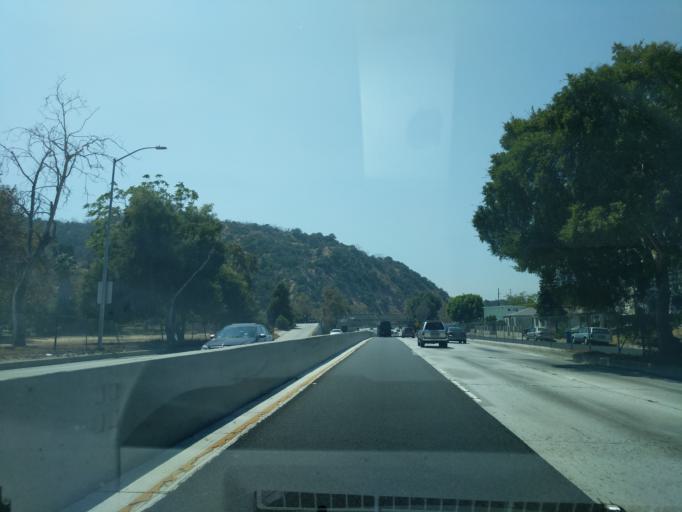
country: US
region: California
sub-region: Los Angeles County
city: South Pasadena
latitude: 34.1051
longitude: -118.1894
